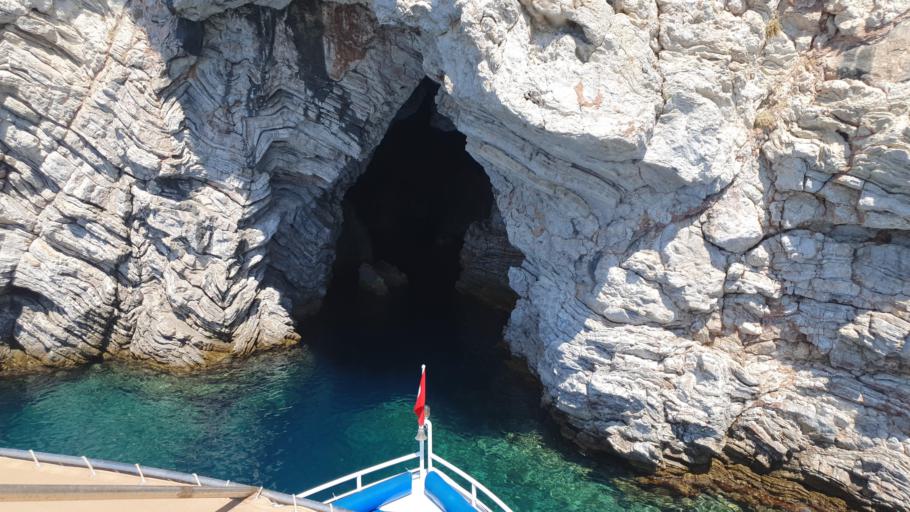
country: TR
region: Mugla
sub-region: Marmaris
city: Marmaris
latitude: 36.7921
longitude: 28.2844
